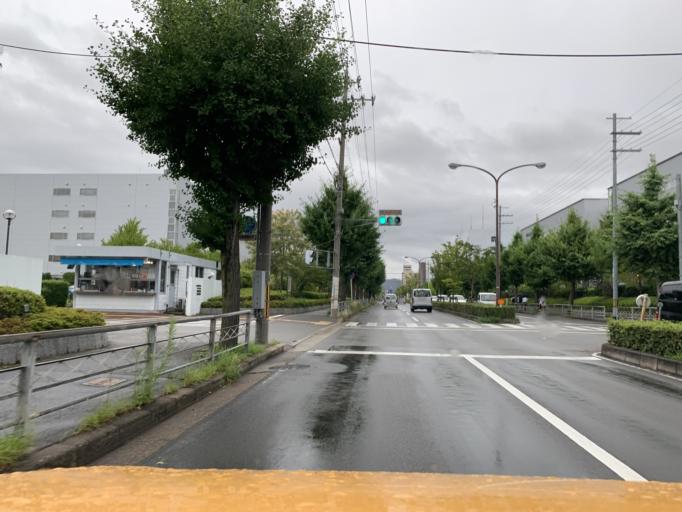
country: JP
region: Kyoto
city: Kyoto
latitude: 35.0110
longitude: 135.7268
